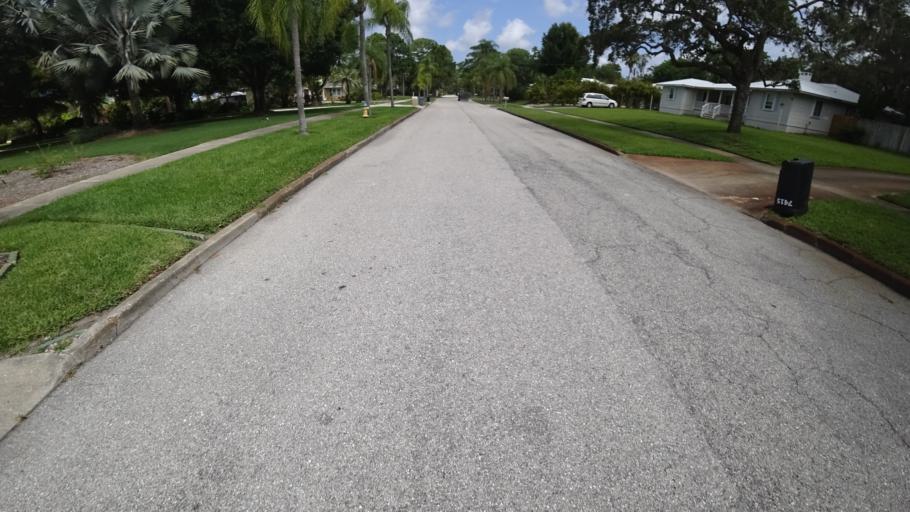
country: US
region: Florida
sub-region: Manatee County
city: Whitfield
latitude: 27.4085
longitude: -82.5751
